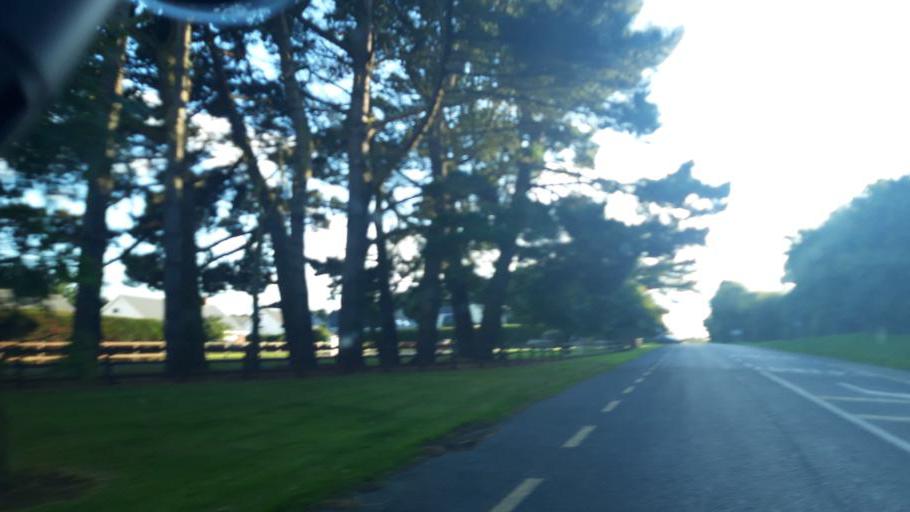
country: IE
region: Leinster
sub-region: Lu
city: Carlingford
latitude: 54.0195
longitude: -6.1459
